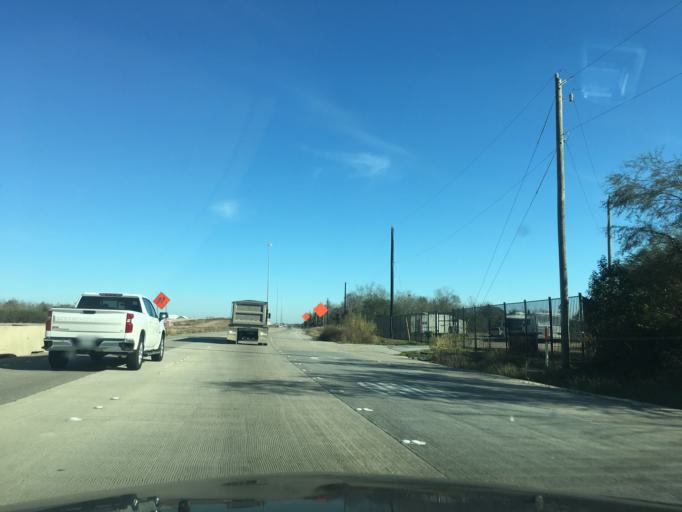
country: US
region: Texas
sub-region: Fort Bend County
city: Rosenberg
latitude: 29.5349
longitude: -95.8518
